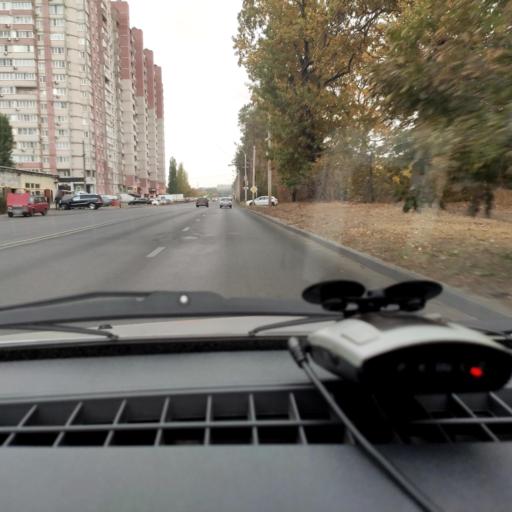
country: RU
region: Voronezj
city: Podgornoye
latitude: 51.7265
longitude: 39.1927
